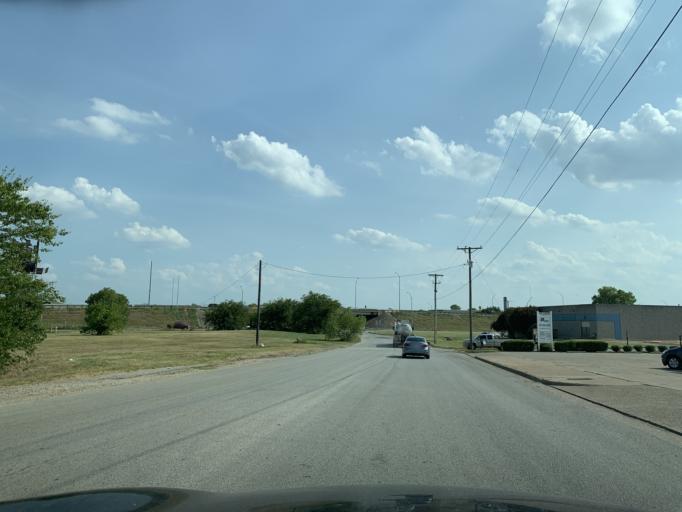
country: US
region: Texas
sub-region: Tarrant County
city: Haltom City
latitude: 32.7940
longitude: -97.2443
